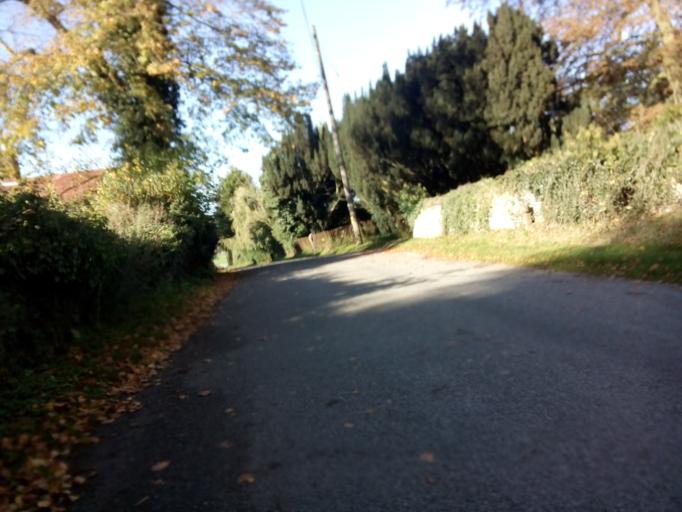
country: GB
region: England
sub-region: Suffolk
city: Lavenham
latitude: 52.0605
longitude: 0.7874
